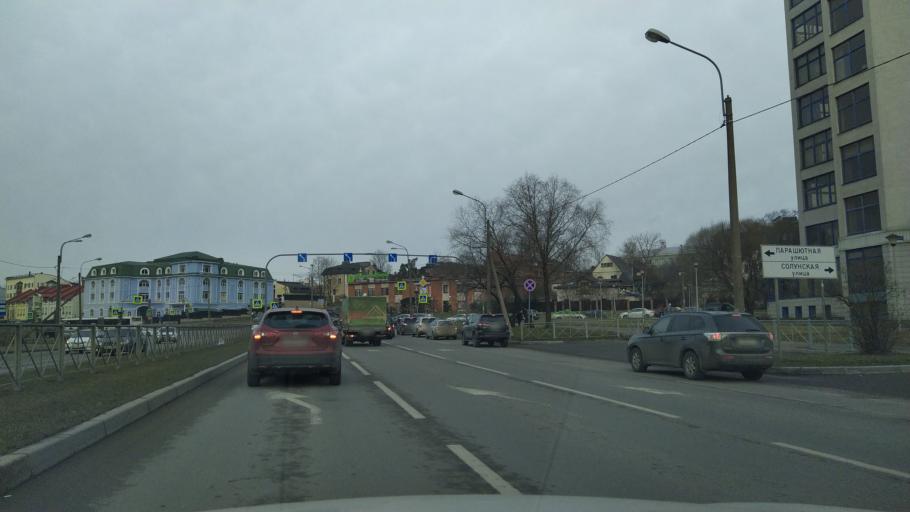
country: RU
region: St.-Petersburg
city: Kolomyagi
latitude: 60.0144
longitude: 30.2941
